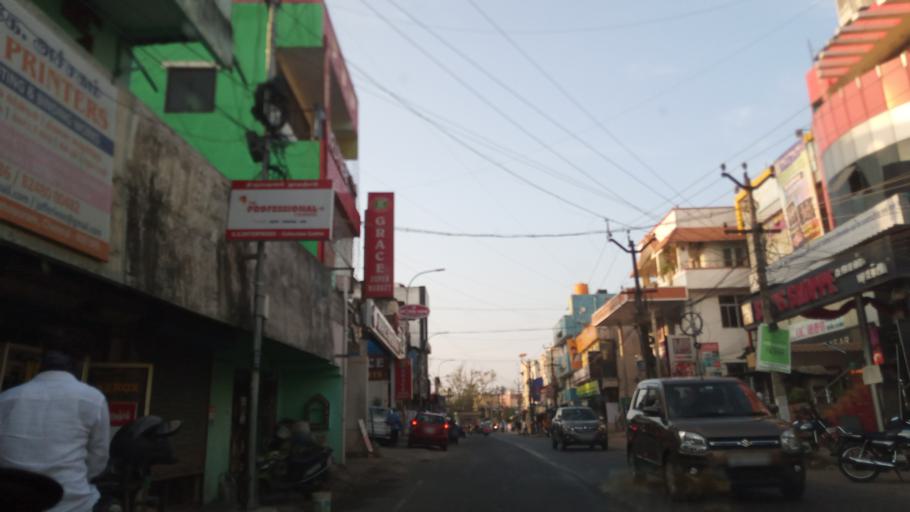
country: IN
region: Tamil Nadu
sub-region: Kancheepuram
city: Manappakkam
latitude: 13.0298
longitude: 80.1836
